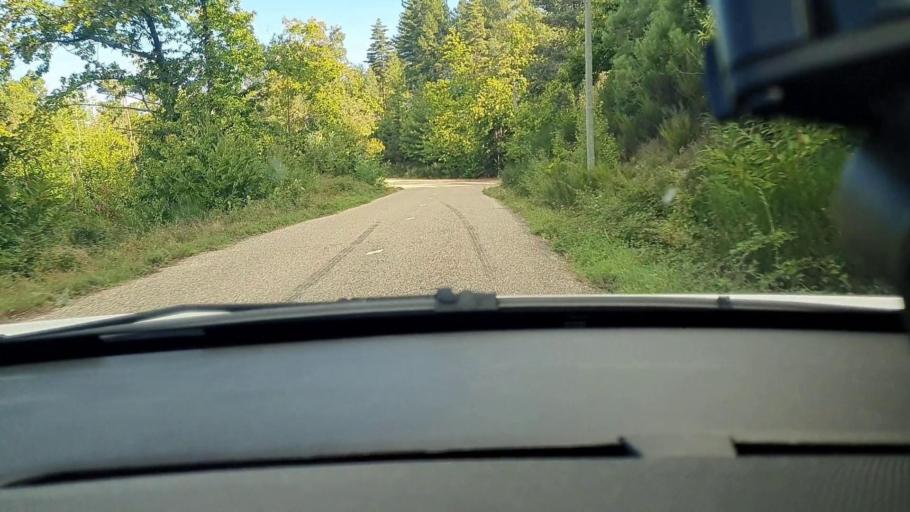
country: FR
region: Rhone-Alpes
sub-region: Departement de l'Ardeche
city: Les Vans
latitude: 44.3940
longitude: 3.9923
